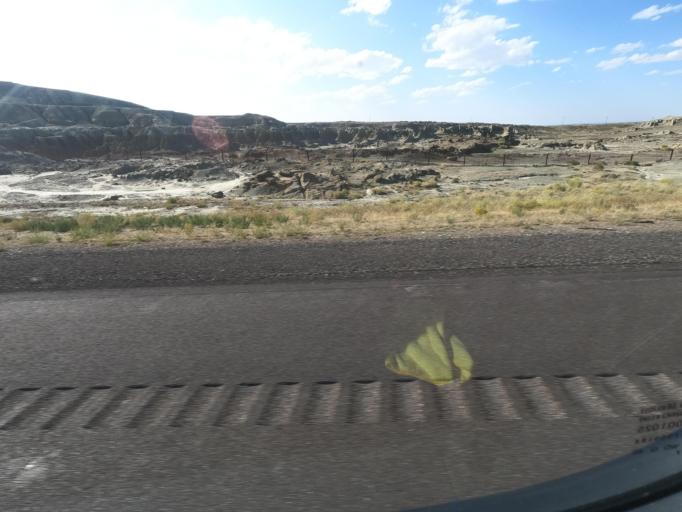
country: US
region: Wyoming
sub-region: Uinta County
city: Lyman
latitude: 41.4159
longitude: -110.1425
